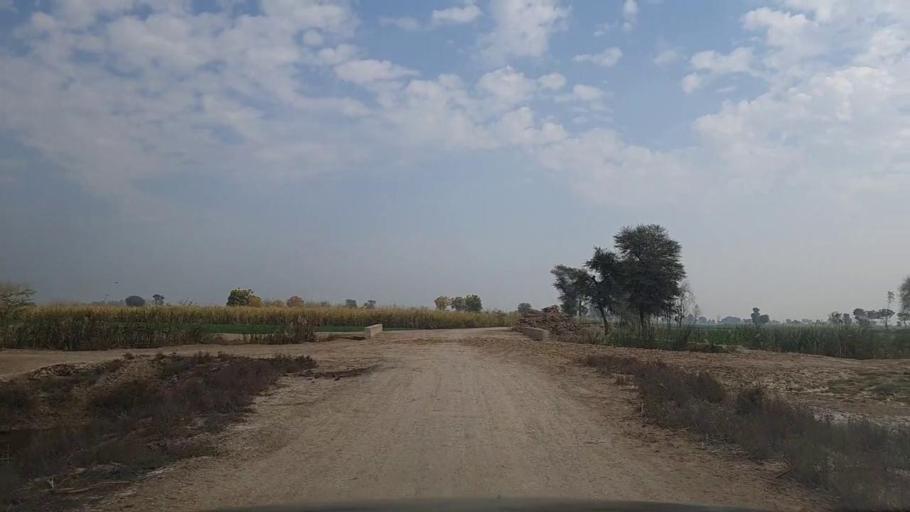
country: PK
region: Sindh
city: Daur
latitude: 26.3986
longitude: 68.3470
